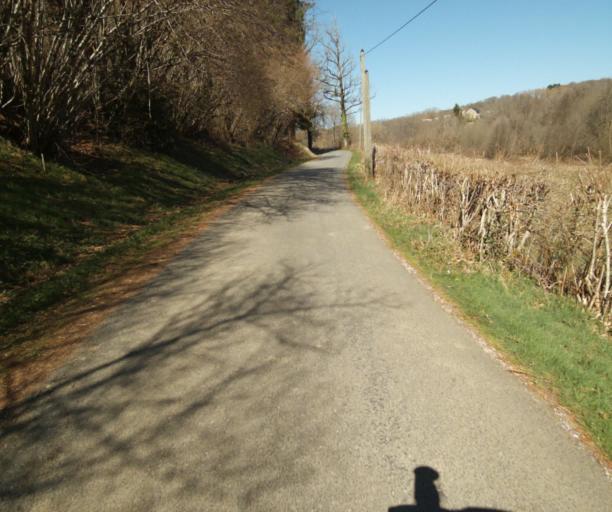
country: FR
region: Limousin
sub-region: Departement de la Correze
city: Saint-Clement
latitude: 45.3233
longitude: 1.7043
